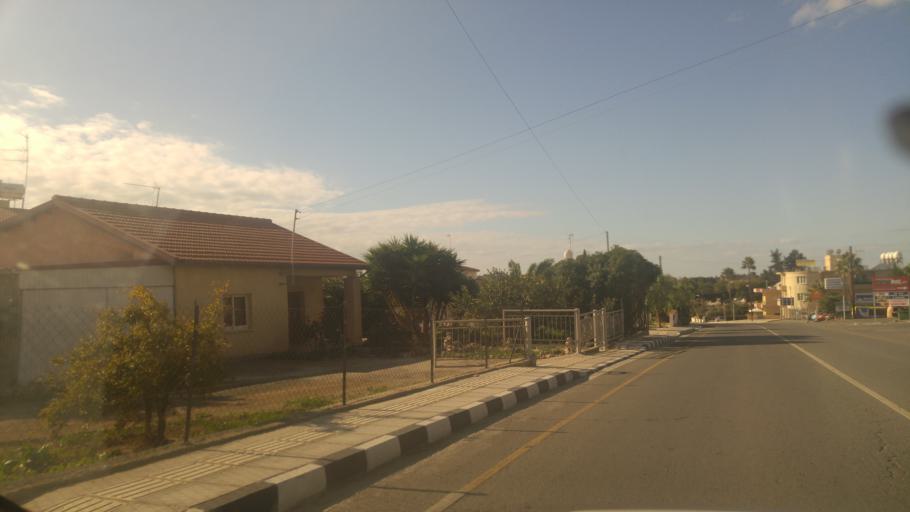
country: CY
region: Larnaka
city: Kolossi
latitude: 34.6730
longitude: 32.9392
